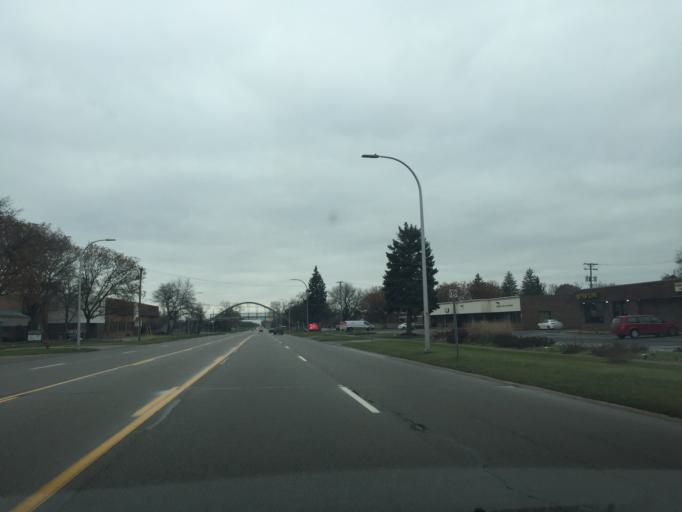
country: US
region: Michigan
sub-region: Oakland County
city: Farmington
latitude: 42.4381
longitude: -83.3365
